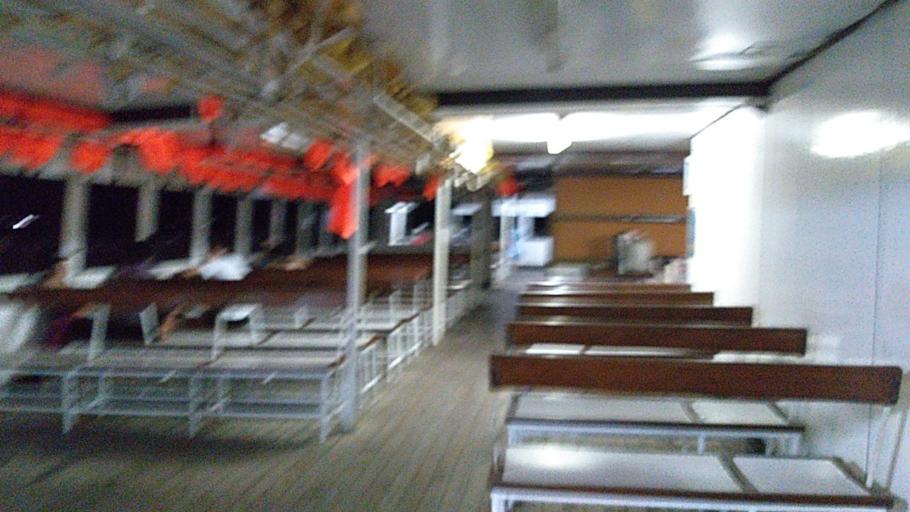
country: TH
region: Trat
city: Laem Ngop
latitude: 12.1751
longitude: 102.2984
